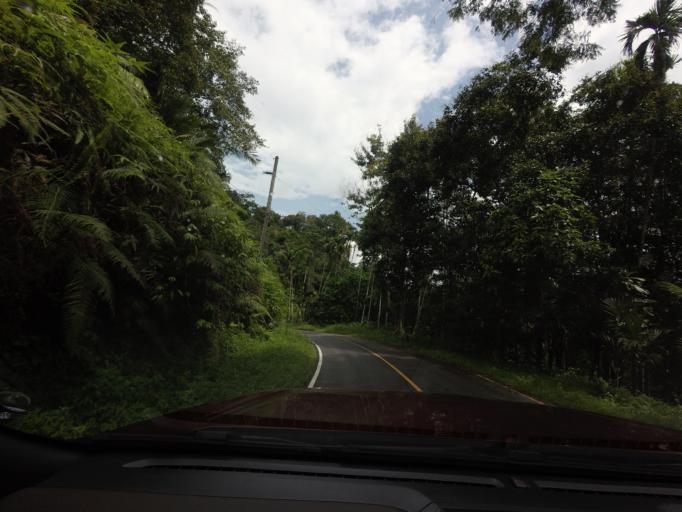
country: TH
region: Narathiwat
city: Sukhirin
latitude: 5.9405
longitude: 101.6521
